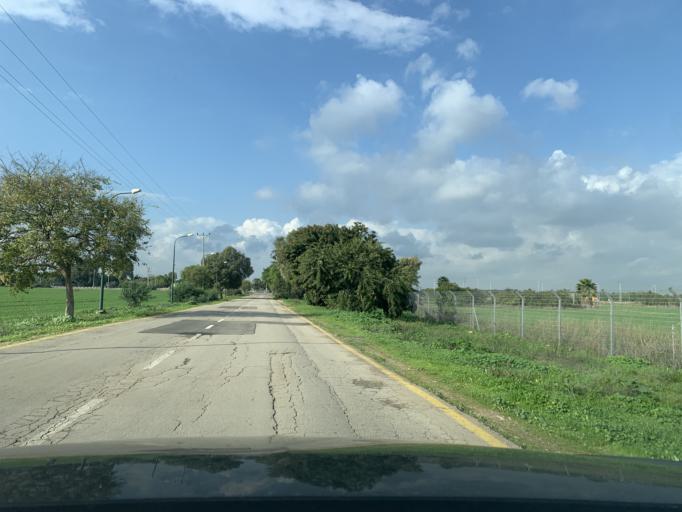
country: IL
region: Central District
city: Petah Tiqwa
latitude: 32.0964
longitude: 34.9175
